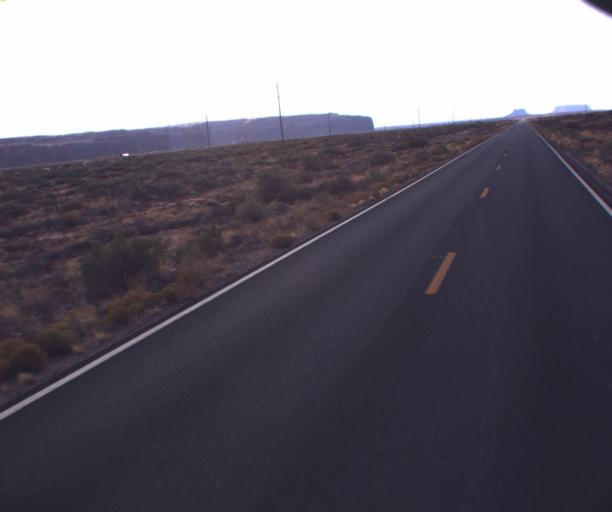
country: US
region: Arizona
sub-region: Apache County
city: Many Farms
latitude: 36.6591
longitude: -109.5951
